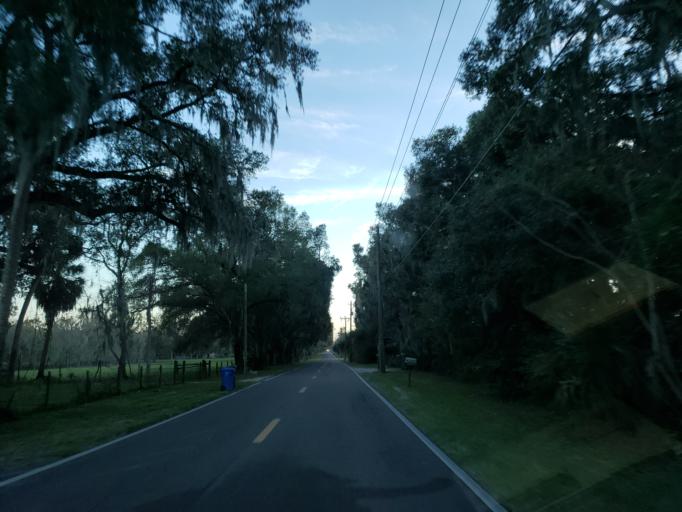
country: US
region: Florida
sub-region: Hillsborough County
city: Fish Hawk
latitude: 27.8469
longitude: -82.1745
